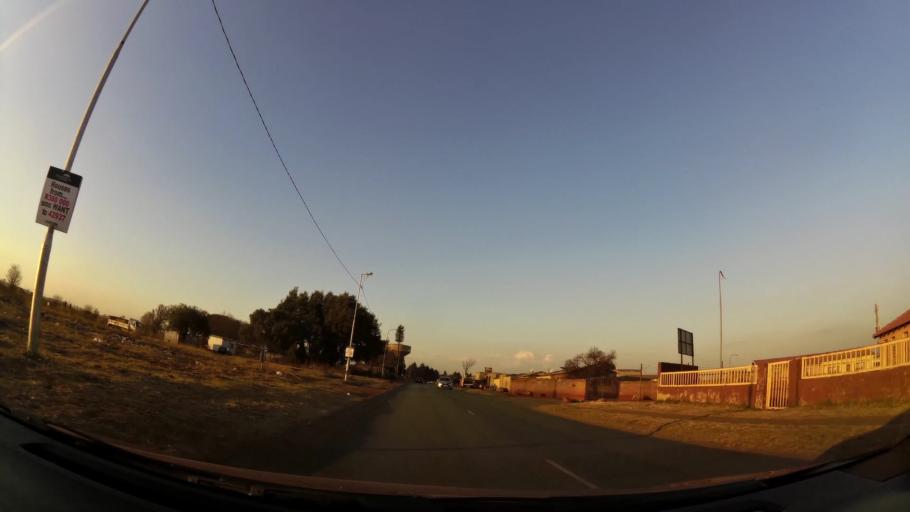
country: ZA
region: Gauteng
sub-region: City of Johannesburg Metropolitan Municipality
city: Soweto
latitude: -26.2176
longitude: 27.8582
